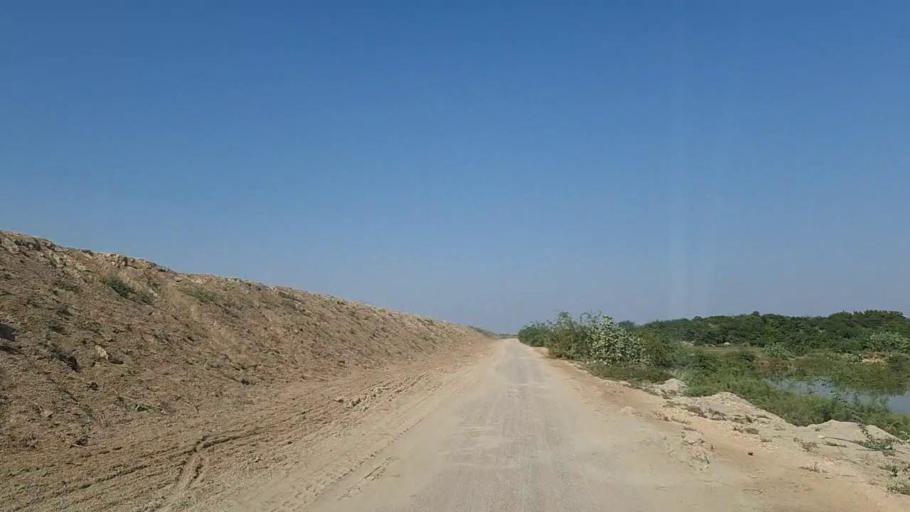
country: PK
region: Sindh
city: Chuhar Jamali
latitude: 24.5690
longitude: 68.0298
